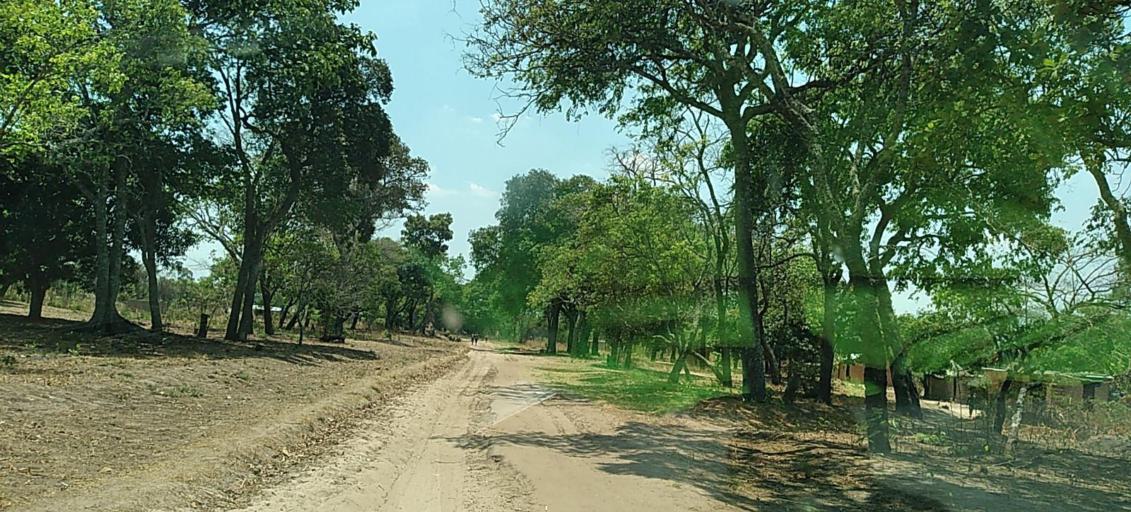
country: CD
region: Katanga
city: Kolwezi
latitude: -11.3753
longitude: 25.2158
